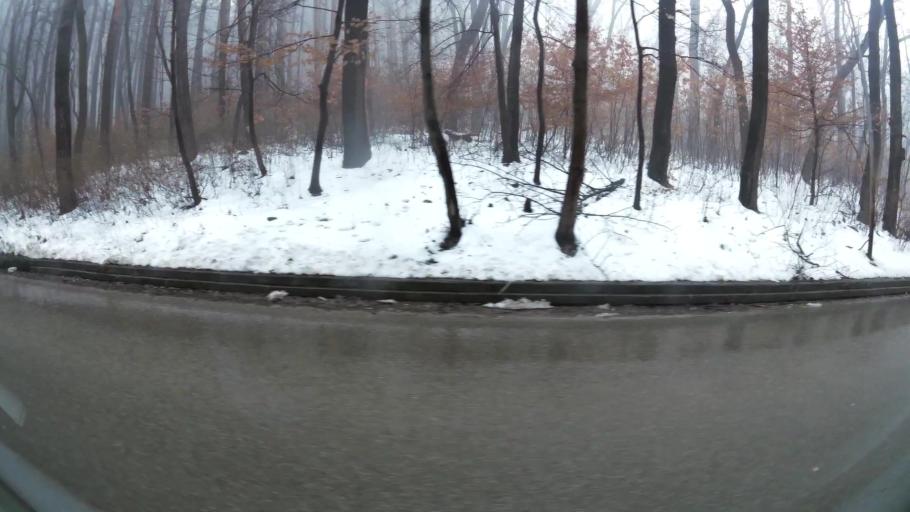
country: BG
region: Sofia-Capital
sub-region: Stolichna Obshtina
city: Sofia
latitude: 42.6571
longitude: 23.2424
